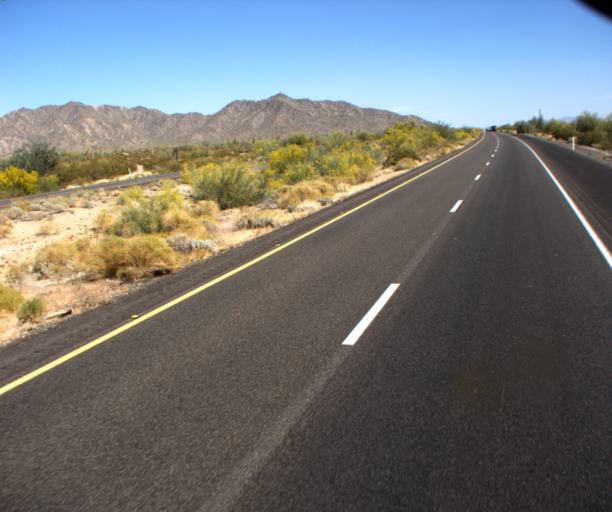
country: US
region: Arizona
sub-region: Maricopa County
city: Gila Bend
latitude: 32.8713
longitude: -112.4375
